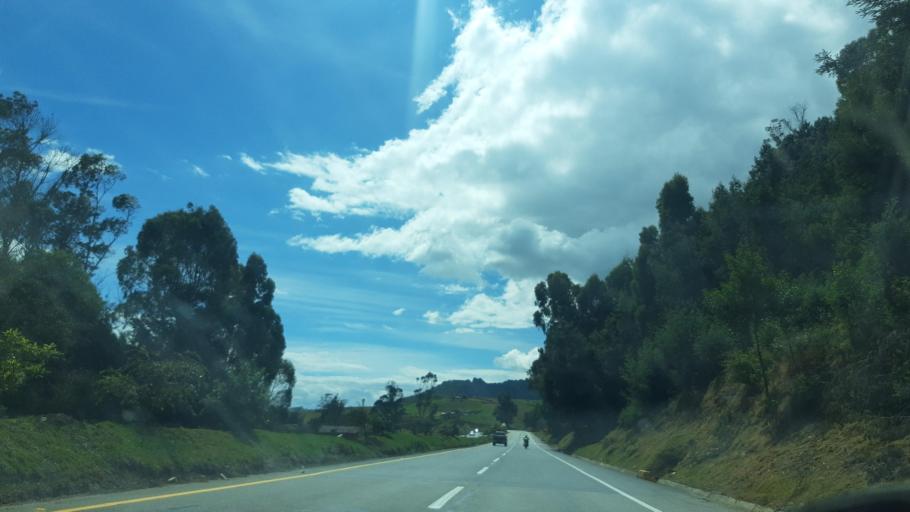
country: CO
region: Cundinamarca
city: Villapinzon
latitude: 5.2517
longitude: -73.5901
